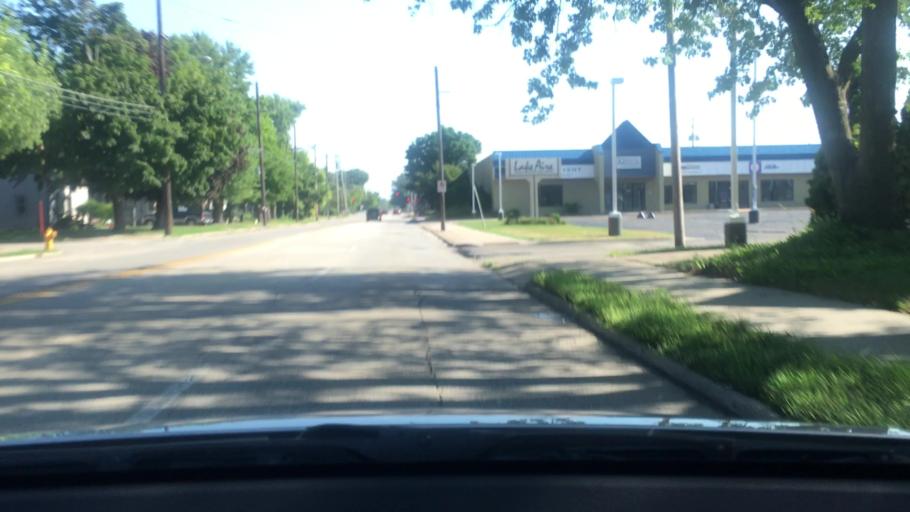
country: US
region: Wisconsin
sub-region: Winnebago County
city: Oshkosh
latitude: 43.9944
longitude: -88.5426
